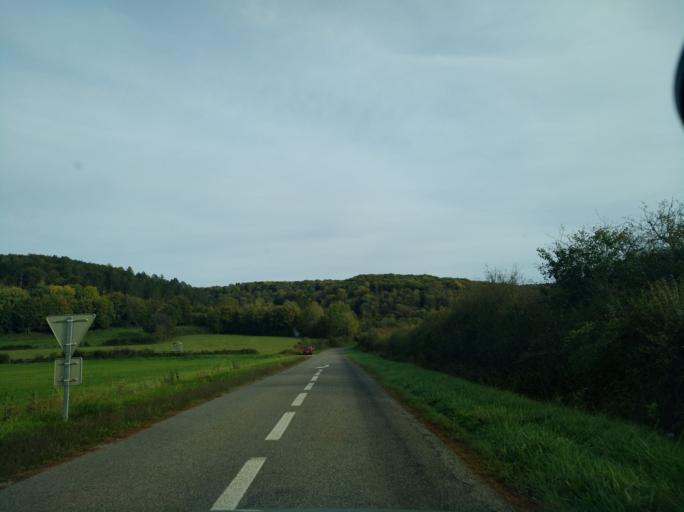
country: FR
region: Bourgogne
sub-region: Departement de Saone-et-Loire
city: Cuiseaux
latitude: 46.4828
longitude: 5.4676
